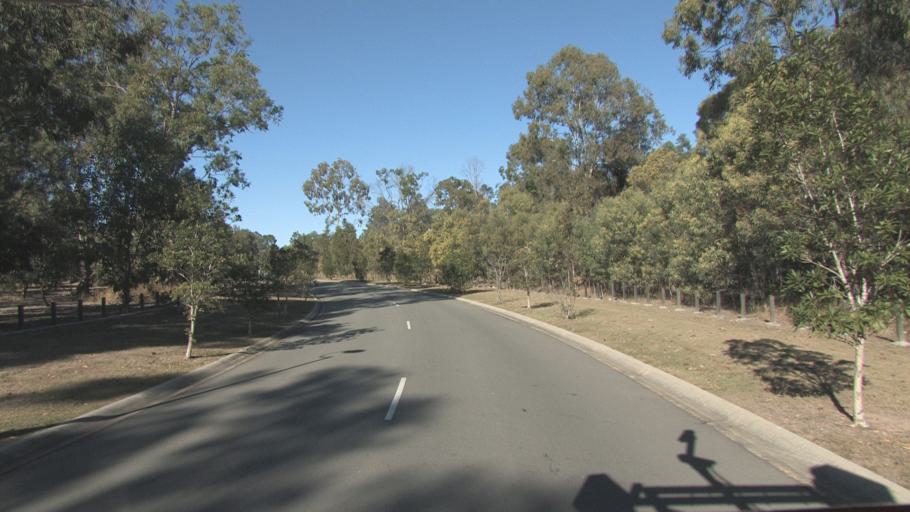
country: AU
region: Queensland
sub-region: Logan
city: North Maclean
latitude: -27.7543
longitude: 152.9673
